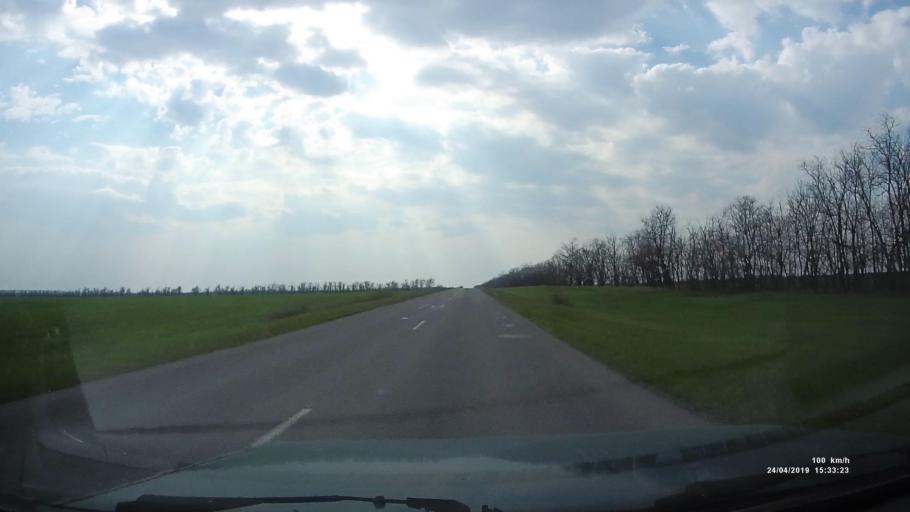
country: RU
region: Rostov
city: Remontnoye
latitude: 46.5995
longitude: 42.9396
